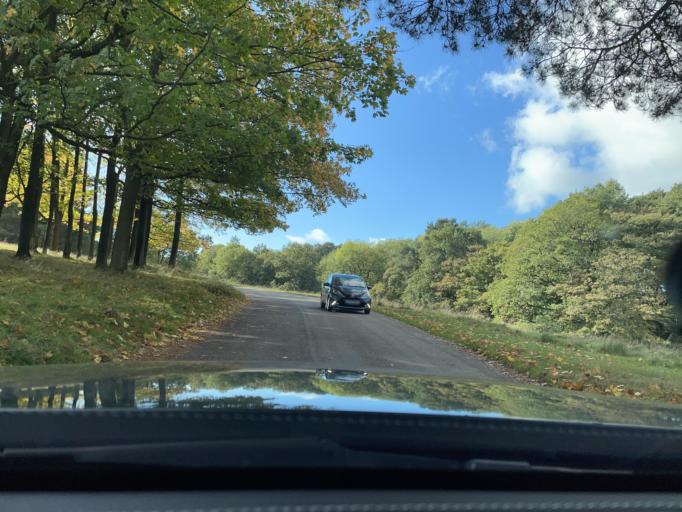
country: GB
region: England
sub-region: Cheshire East
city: Disley
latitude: 53.3524
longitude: -2.0543
